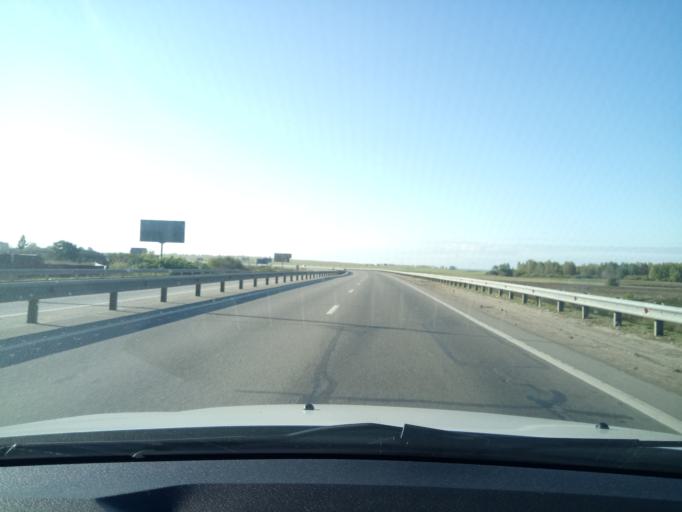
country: RU
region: Nizjnij Novgorod
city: Burevestnik
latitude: 56.1551
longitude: 43.9109
